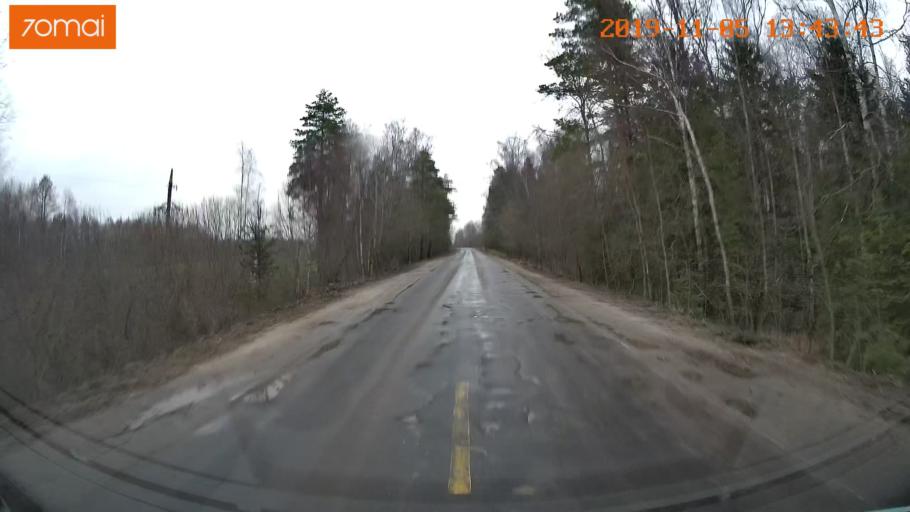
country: RU
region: Ivanovo
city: Shuya
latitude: 56.9755
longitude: 41.4051
